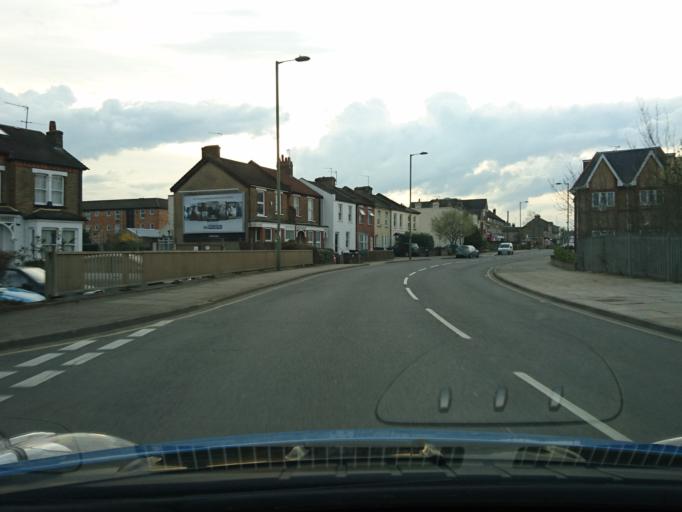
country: GB
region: England
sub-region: Greater London
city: Wood Green
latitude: 51.6228
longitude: -0.1522
